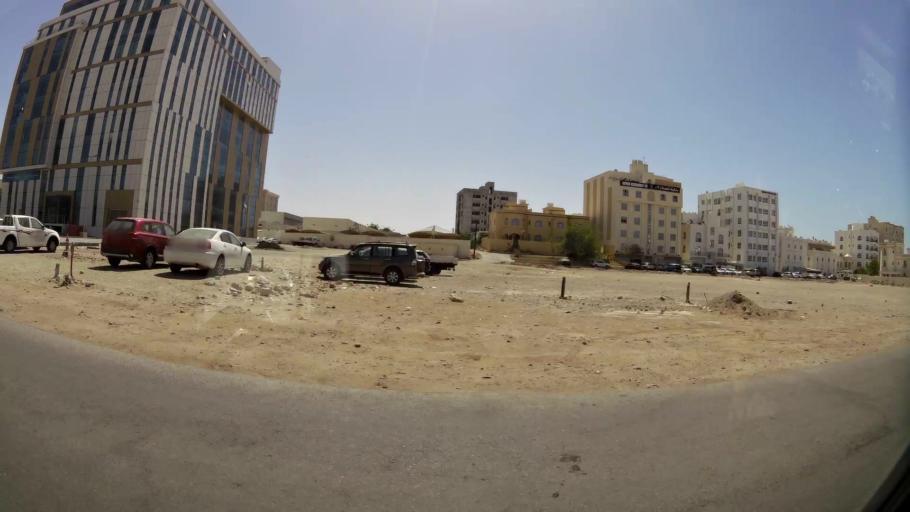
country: OM
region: Muhafazat Masqat
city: Bawshar
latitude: 23.5906
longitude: 58.3608
